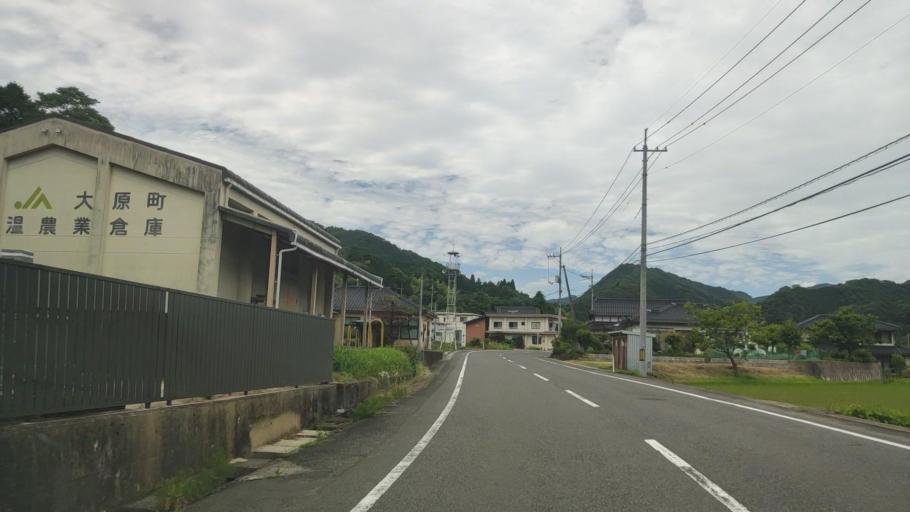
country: JP
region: Hyogo
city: Yamazakicho-nakabirose
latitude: 35.0978
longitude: 134.2967
